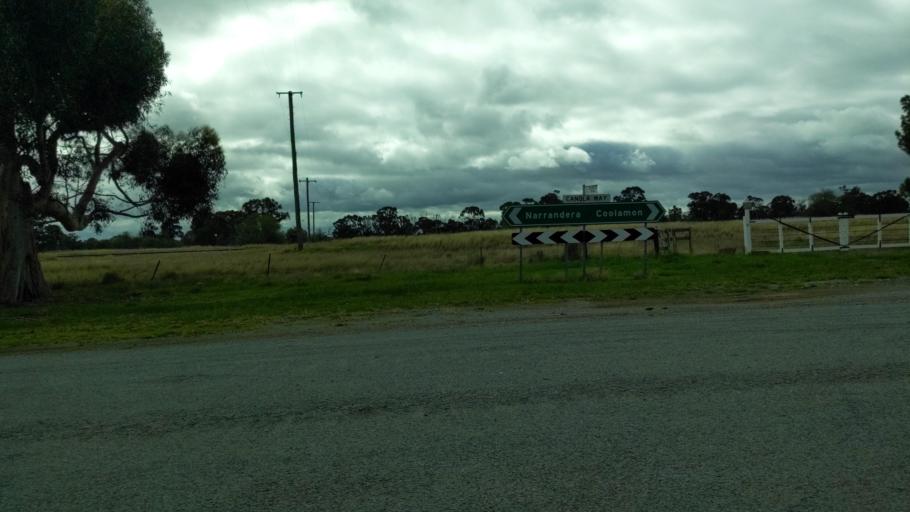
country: AU
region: New South Wales
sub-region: Coolamon
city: Coolamon
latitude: -34.7679
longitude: 146.9189
